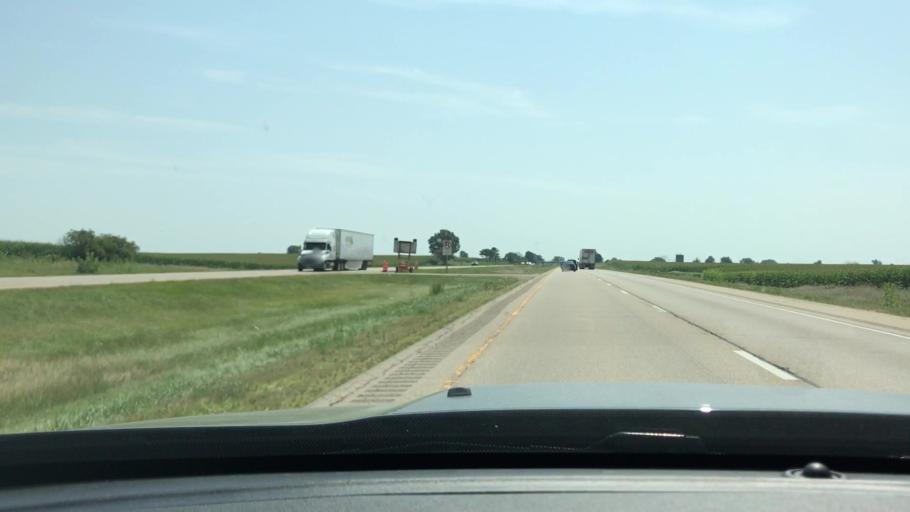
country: US
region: Illinois
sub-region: Bureau County
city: Depue
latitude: 41.3919
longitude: -89.2891
